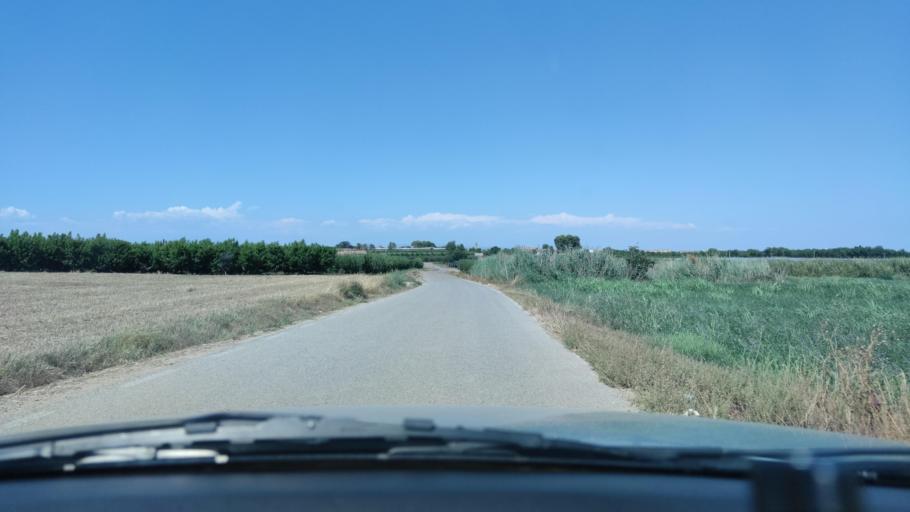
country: ES
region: Catalonia
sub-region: Provincia de Lleida
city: Torrefarrera
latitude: 41.6832
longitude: 0.6182
